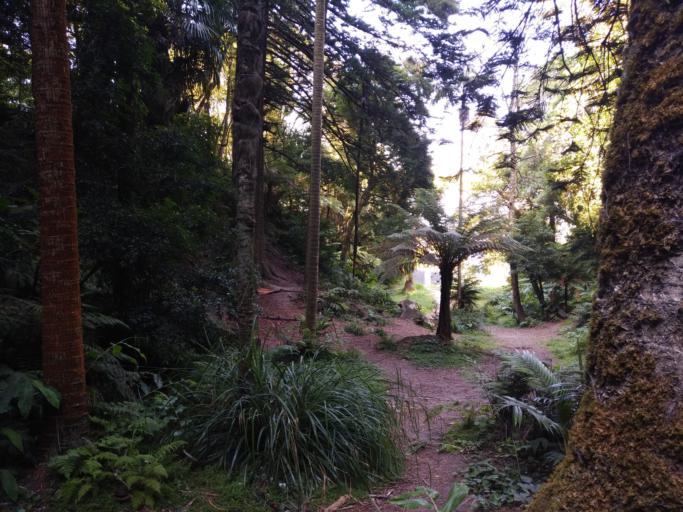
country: PT
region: Azores
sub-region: Povoacao
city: Furnas
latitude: 37.7508
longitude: -25.3388
